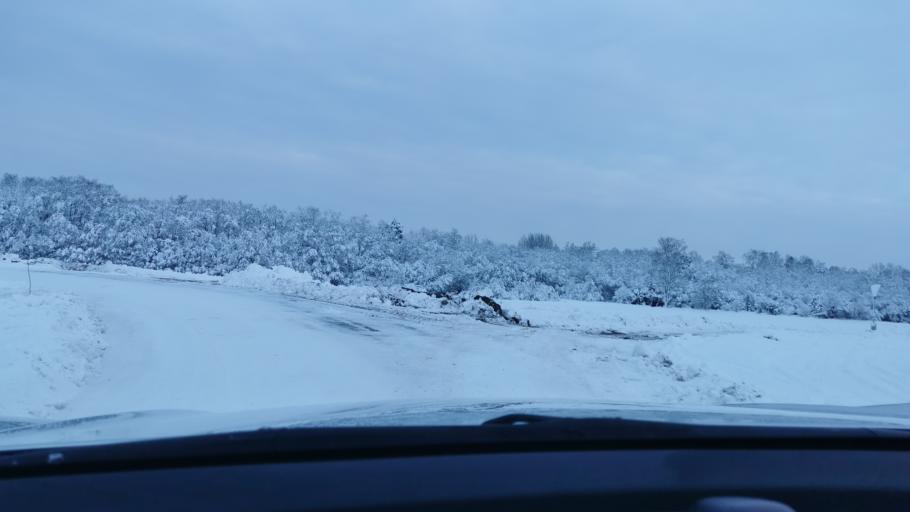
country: EE
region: Laeaene-Virumaa
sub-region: Haljala vald
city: Haljala
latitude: 59.4756
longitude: 26.3645
